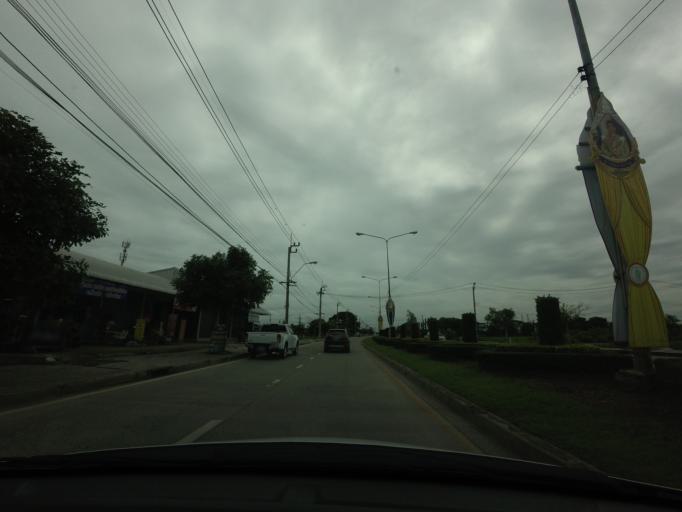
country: TH
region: Pathum Thani
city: Lam Luk Ka
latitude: 13.9115
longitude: 100.7750
